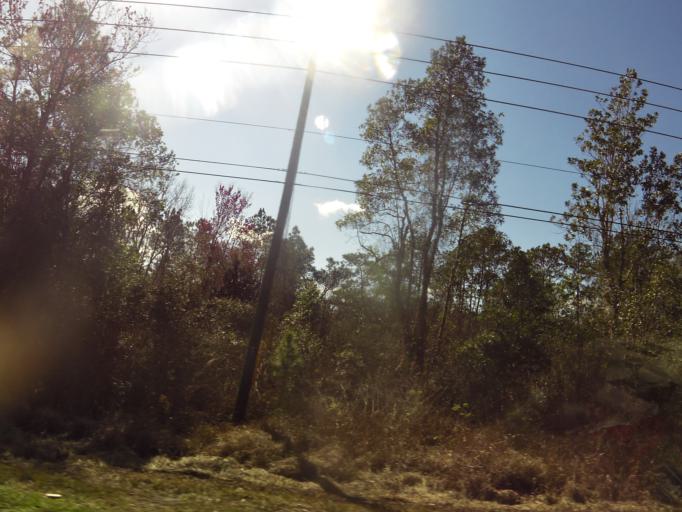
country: US
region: Florida
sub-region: Volusia County
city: Pierson
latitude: 29.2013
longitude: -81.4388
